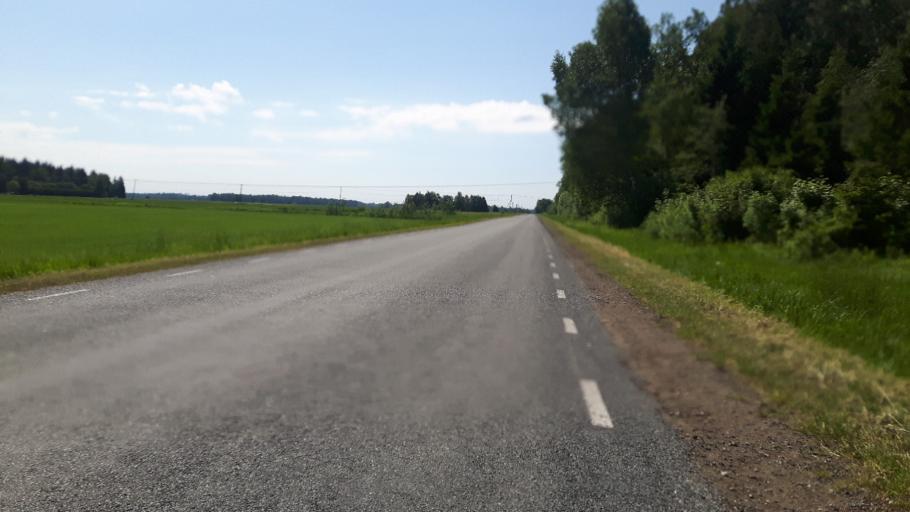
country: EE
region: Paernumaa
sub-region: Vaendra vald (alev)
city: Vandra
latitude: 58.6300
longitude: 25.0208
